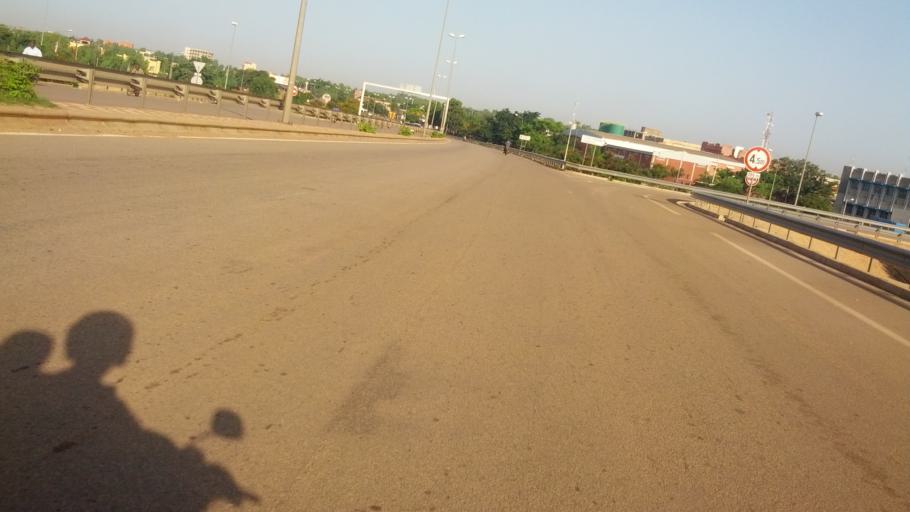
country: BF
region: Centre
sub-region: Kadiogo Province
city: Ouagadougou
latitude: 12.3323
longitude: -1.5030
